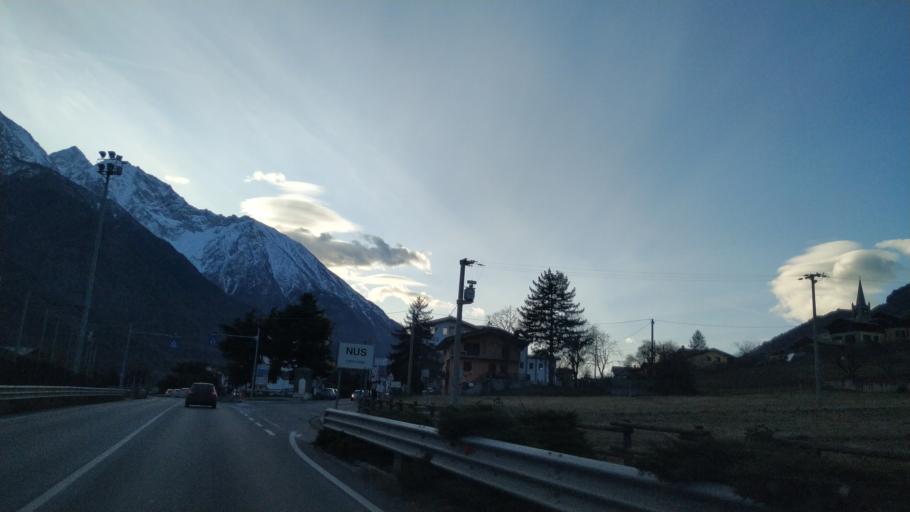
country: IT
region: Aosta Valley
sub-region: Valle d'Aosta
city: Nus
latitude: 45.7416
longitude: 7.4744
